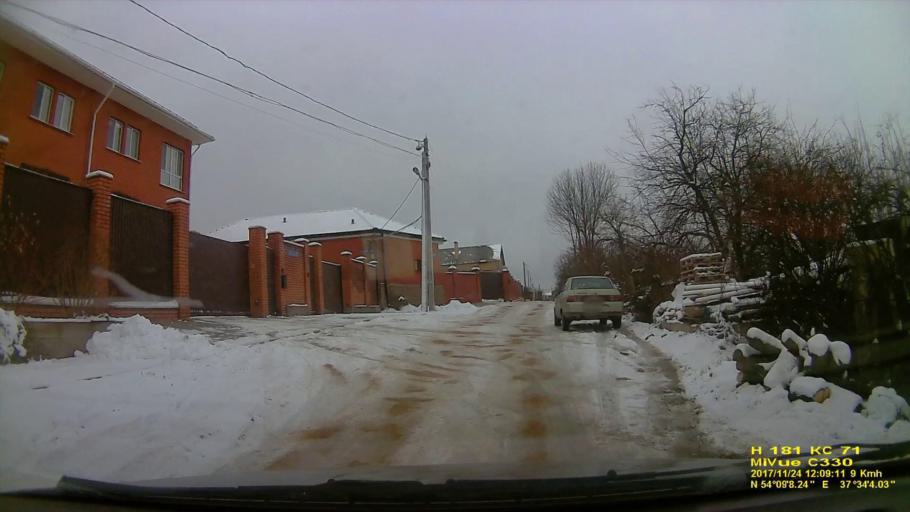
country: RU
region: Tula
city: Mendeleyevskiy
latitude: 54.1522
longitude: 37.5679
